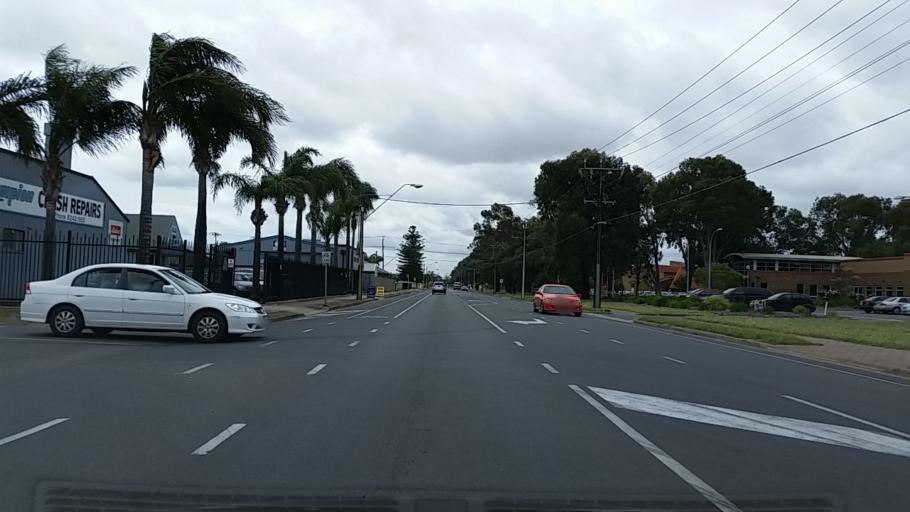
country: AU
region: South Australia
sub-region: Charles Sturt
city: Woodville
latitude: -34.8718
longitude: 138.5660
